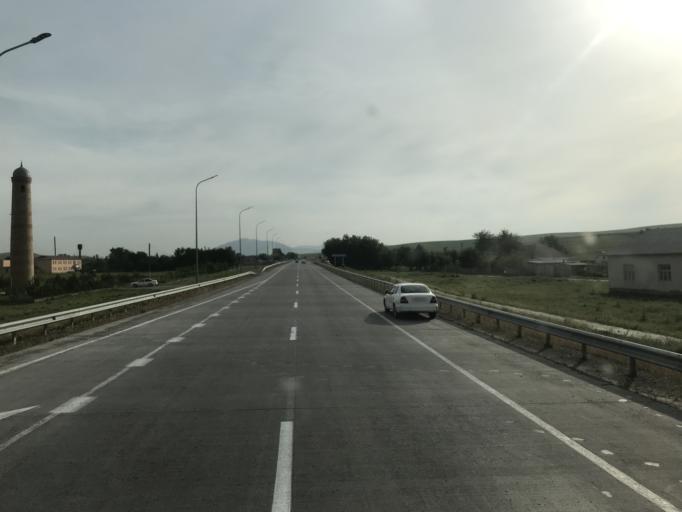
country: KZ
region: Ongtustik Qazaqstan
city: Qazyqurt
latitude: 41.8980
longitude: 69.4561
